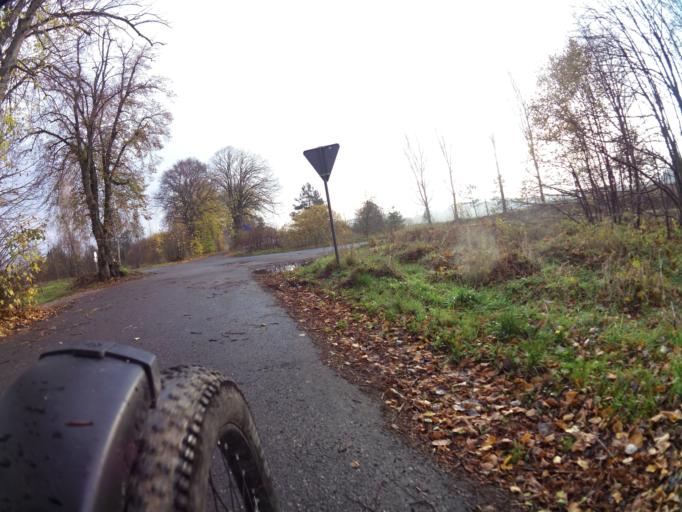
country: PL
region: Pomeranian Voivodeship
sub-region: Powiat wejherowski
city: Gniewino
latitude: 54.7134
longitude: 18.0945
